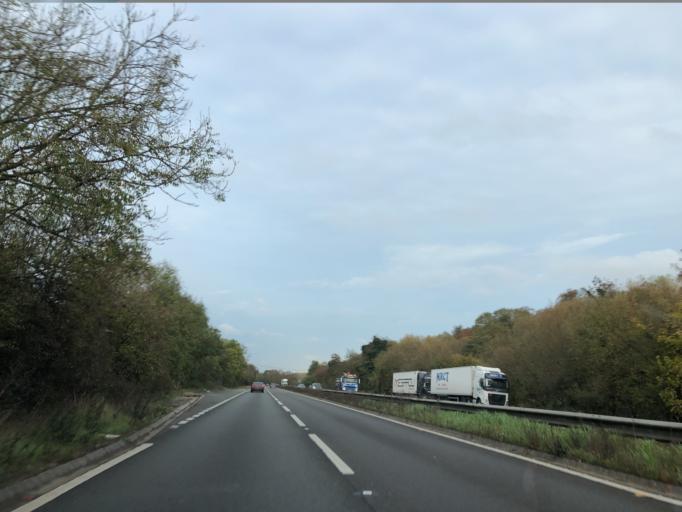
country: GB
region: England
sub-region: Royal Borough of Windsor and Maidenhead
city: Bisham
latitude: 51.5570
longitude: -0.7712
